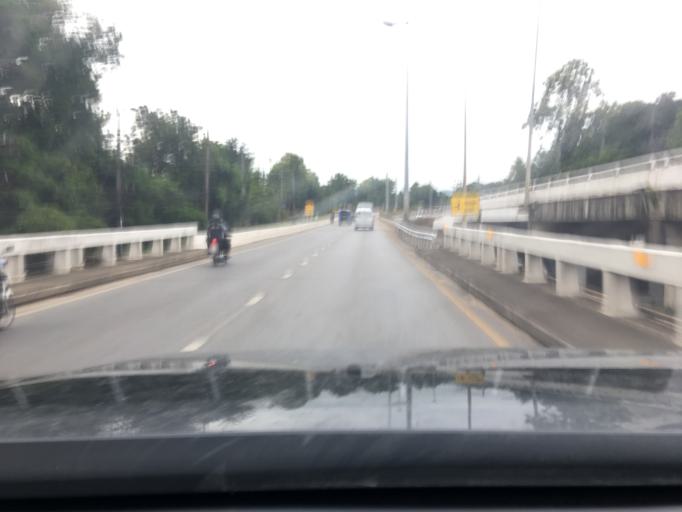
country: TH
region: Chiang Rai
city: Chiang Rai
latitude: 19.9207
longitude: 99.8462
